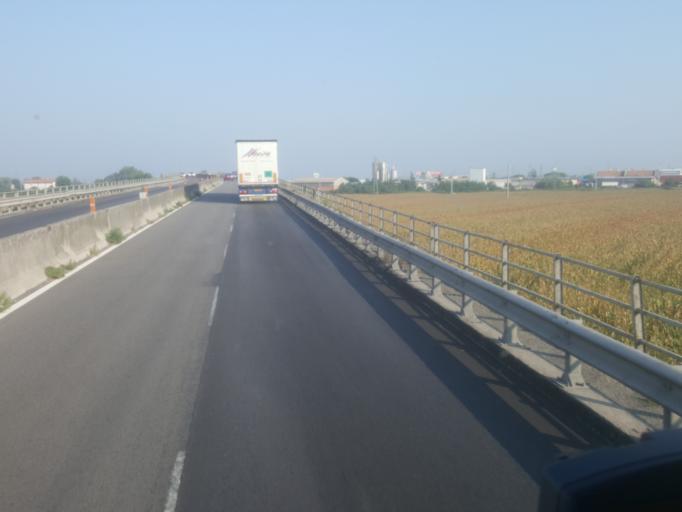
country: IT
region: Emilia-Romagna
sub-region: Provincia di Ravenna
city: Fornace Zarattini
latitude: 44.4192
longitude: 12.1662
